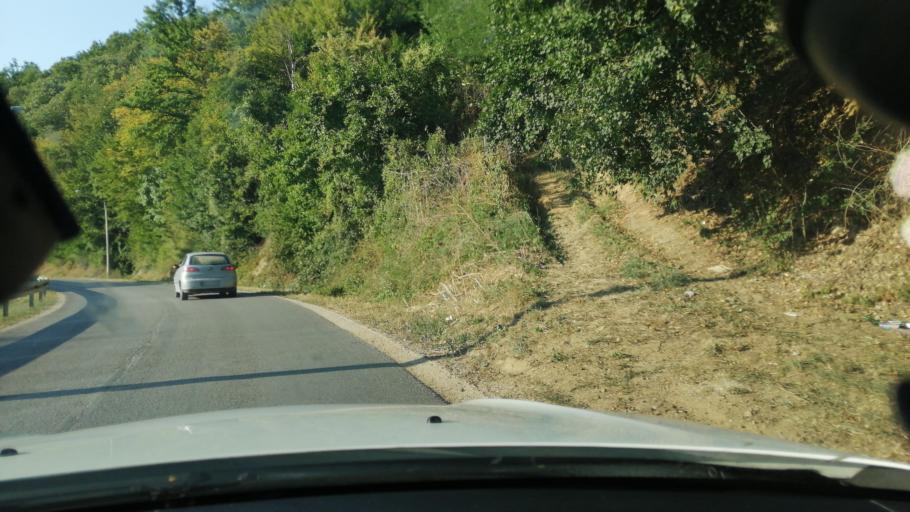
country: RS
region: Central Serbia
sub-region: Moravicki Okrug
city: Lucani
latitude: 43.7756
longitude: 20.2332
